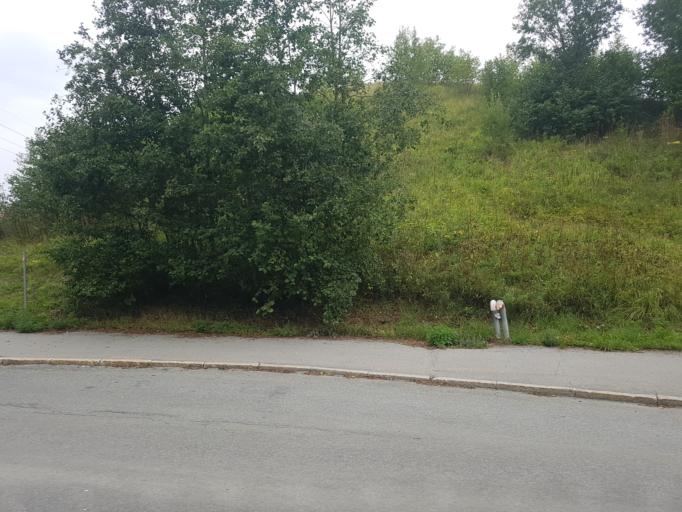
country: NO
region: Sor-Trondelag
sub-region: Trondheim
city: Trondheim
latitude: 63.3880
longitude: 10.3942
